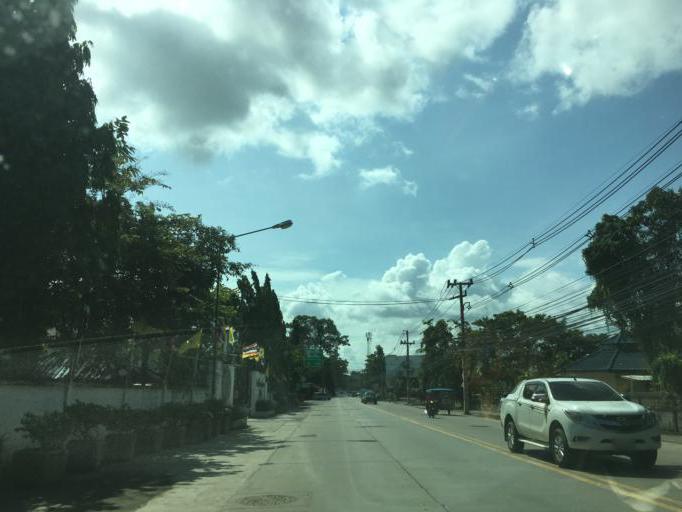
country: TH
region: Chon Buri
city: Phatthaya
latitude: 12.8902
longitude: 100.8922
